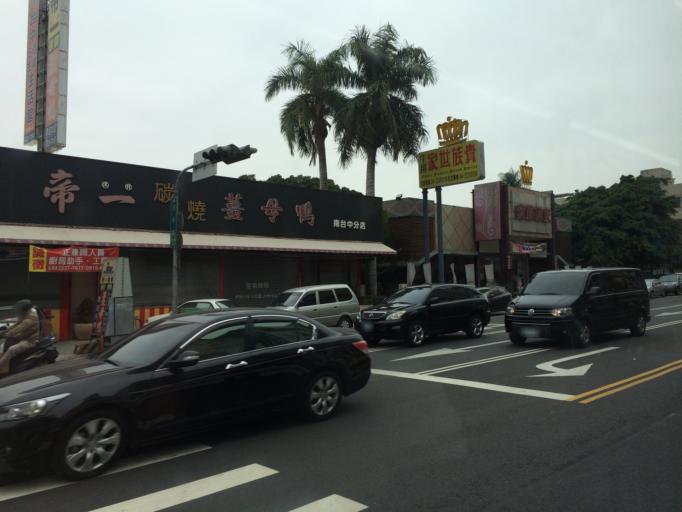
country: TW
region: Taiwan
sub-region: Taichung City
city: Taichung
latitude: 24.1320
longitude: 120.6842
